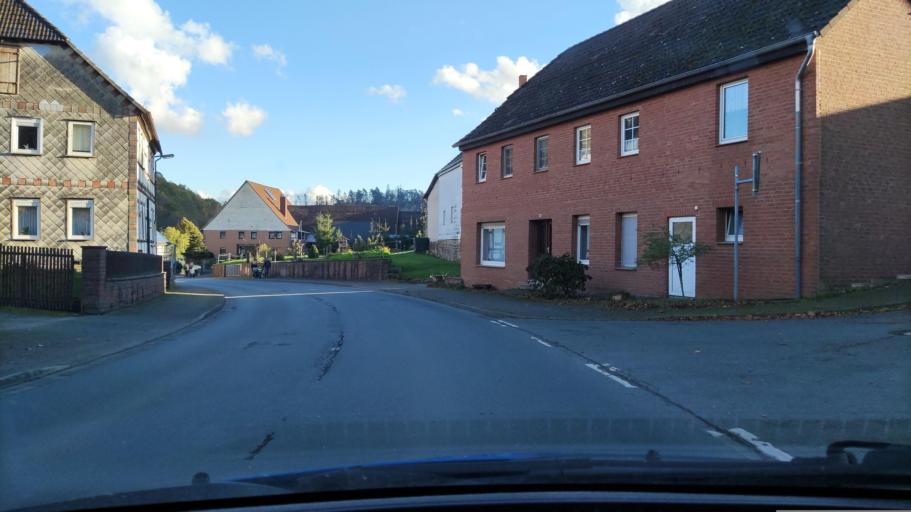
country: DE
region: Lower Saxony
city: Heinade
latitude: 51.8236
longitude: 9.6386
